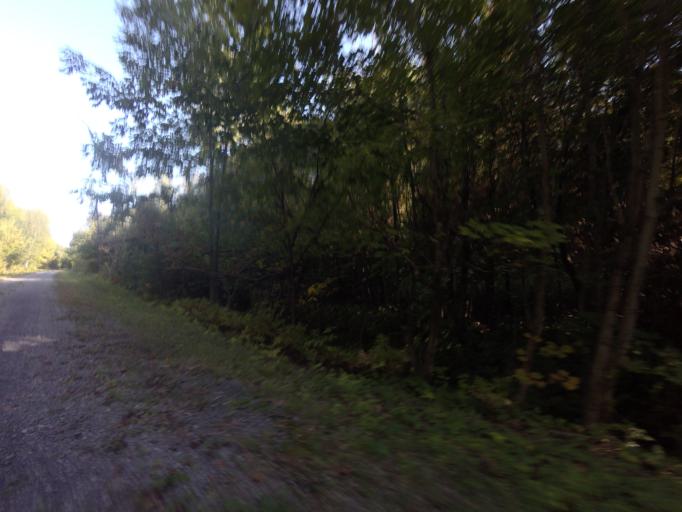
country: CA
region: Ontario
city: Hawkesbury
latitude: 45.5373
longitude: -74.6073
